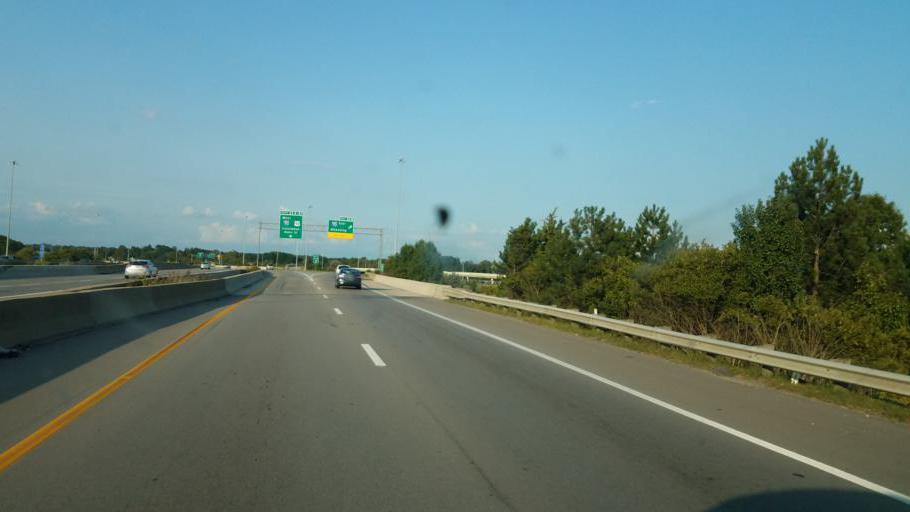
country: US
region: Ohio
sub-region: Franklin County
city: Blacklick Estates
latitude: 39.9319
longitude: -82.8553
